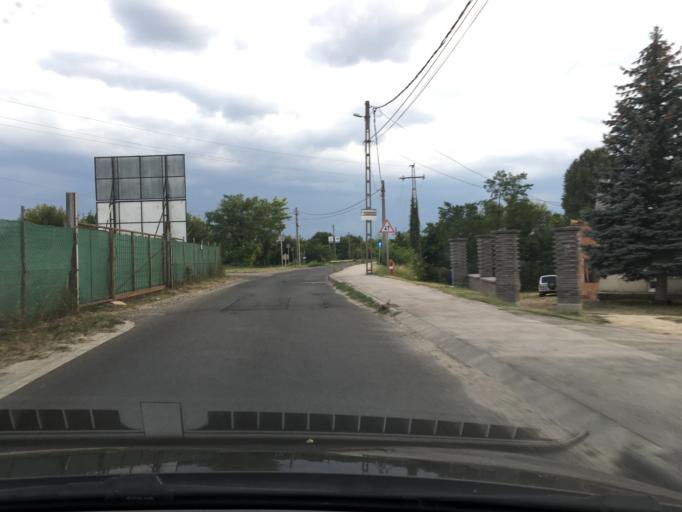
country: HU
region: Pest
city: Veresegyhaz
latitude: 47.6389
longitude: 19.3029
